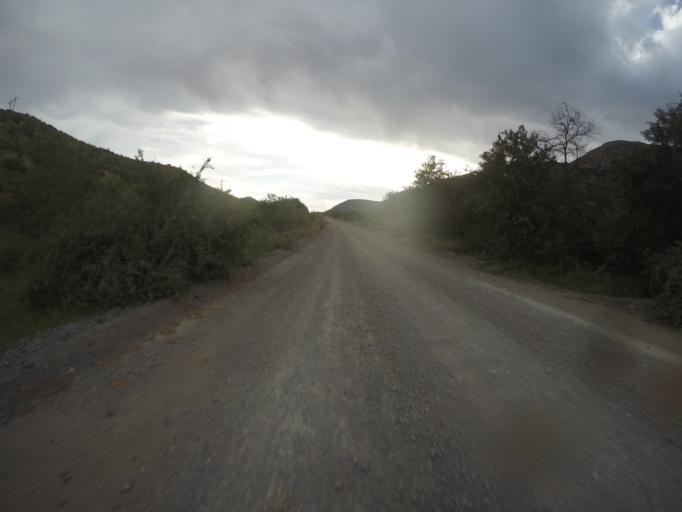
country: ZA
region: Eastern Cape
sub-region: Cacadu District Municipality
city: Willowmore
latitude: -33.5213
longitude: 23.8374
